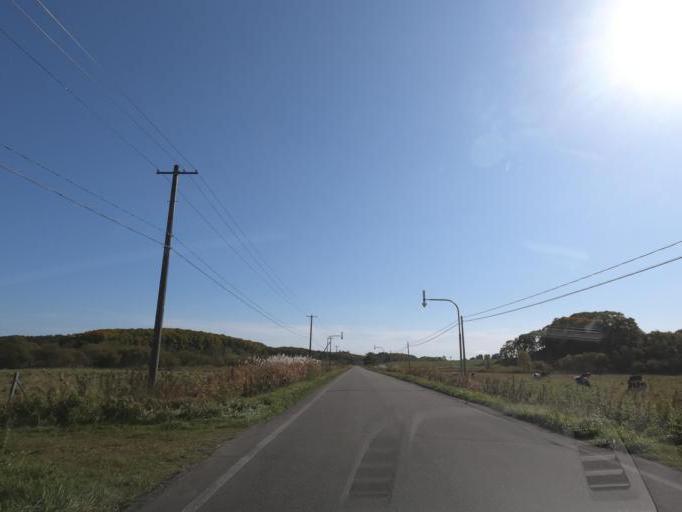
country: JP
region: Hokkaido
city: Obihiro
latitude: 42.7122
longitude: 143.4604
